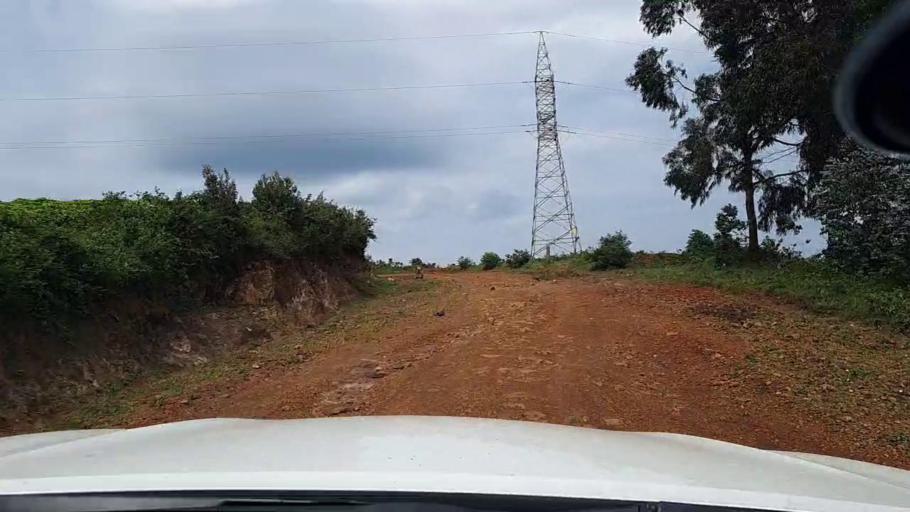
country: RW
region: Western Province
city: Kibuye
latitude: -2.1349
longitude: 29.3760
